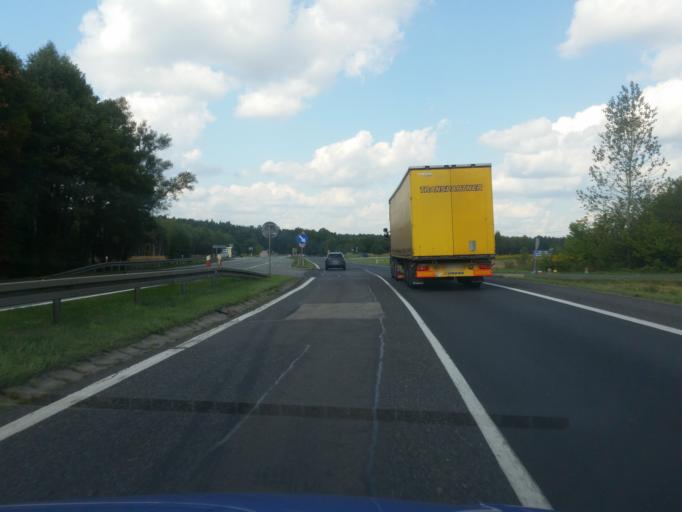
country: PL
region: Silesian Voivodeship
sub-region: Powiat myszkowski
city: Kozieglowy
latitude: 50.5323
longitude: 19.1904
